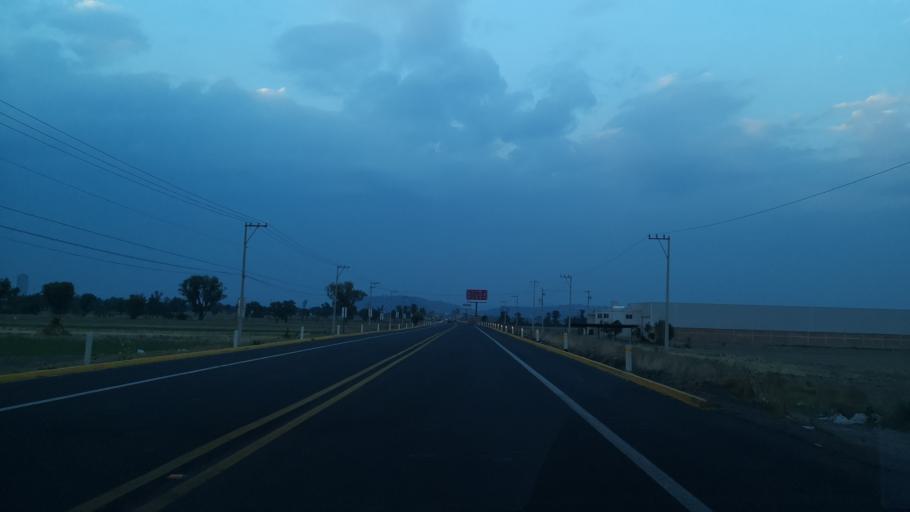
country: MX
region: Puebla
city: Santa Ana Xalmimilulco
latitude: 19.1939
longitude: -98.3663
